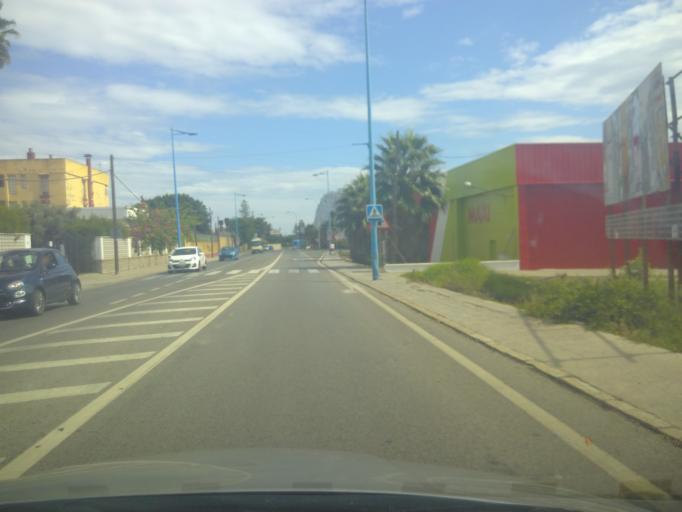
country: ES
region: Andalusia
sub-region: Provincia de Cadiz
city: La Linea de la Concepcion
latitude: 36.1770
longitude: -5.3761
